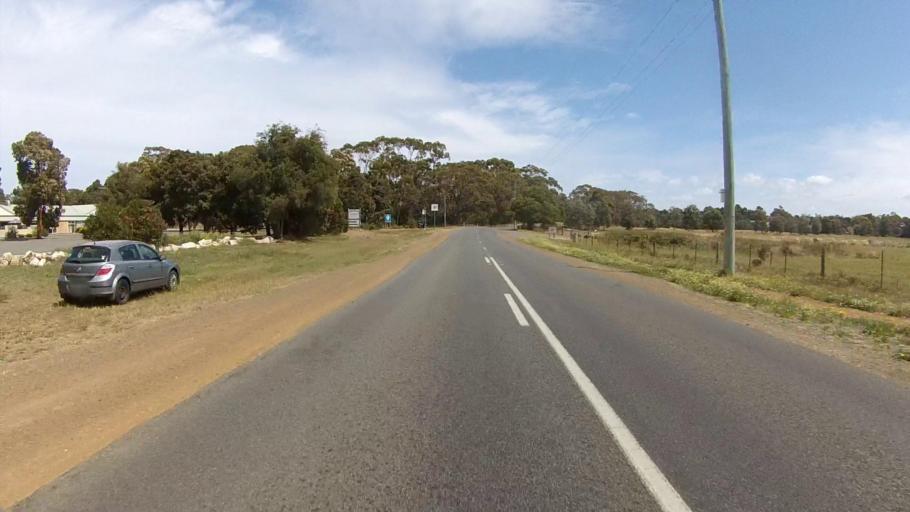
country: AU
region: Tasmania
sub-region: Kingborough
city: Blackmans Bay
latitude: -43.0288
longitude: 147.4294
